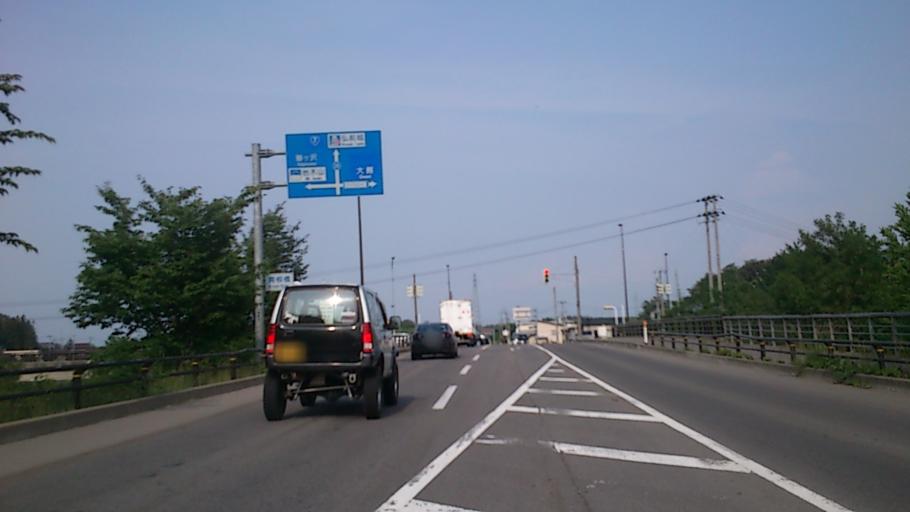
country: JP
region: Aomori
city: Hirosaki
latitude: 40.5916
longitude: 140.4127
